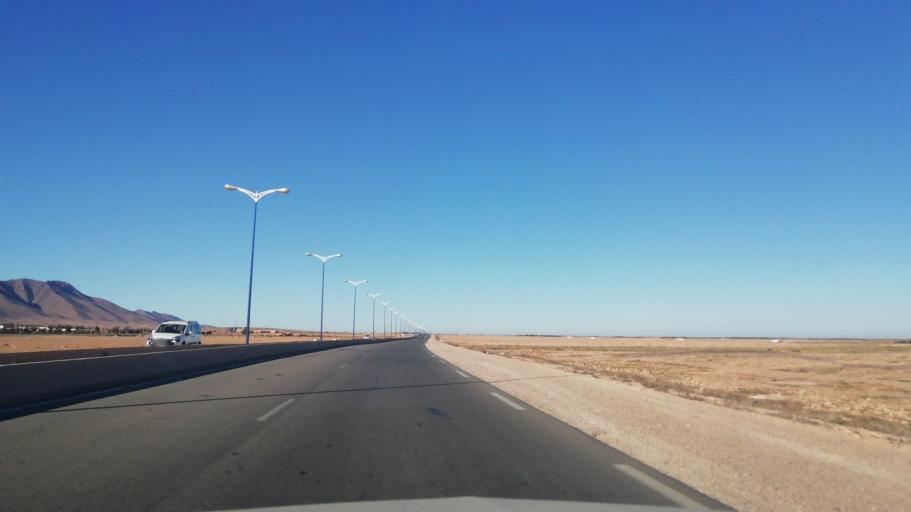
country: DZ
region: Wilaya de Naama
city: Naama
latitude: 33.5692
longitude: -0.2407
